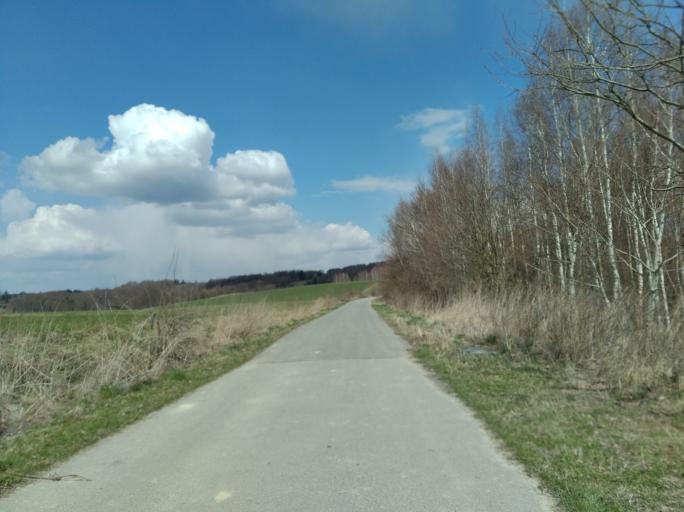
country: PL
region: Subcarpathian Voivodeship
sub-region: Powiat strzyzowski
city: Strzyzow
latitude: 49.9181
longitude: 21.7266
